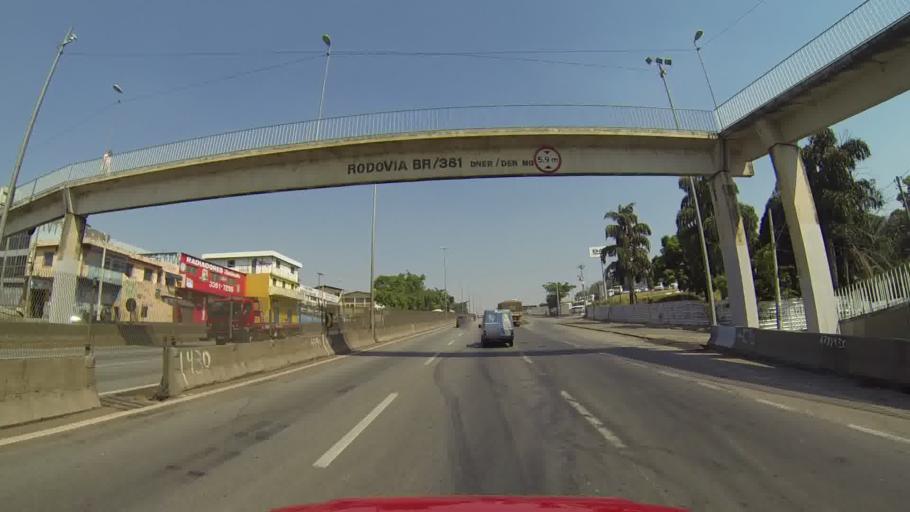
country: BR
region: Minas Gerais
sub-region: Contagem
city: Contagem
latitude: -19.9630
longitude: -44.0488
